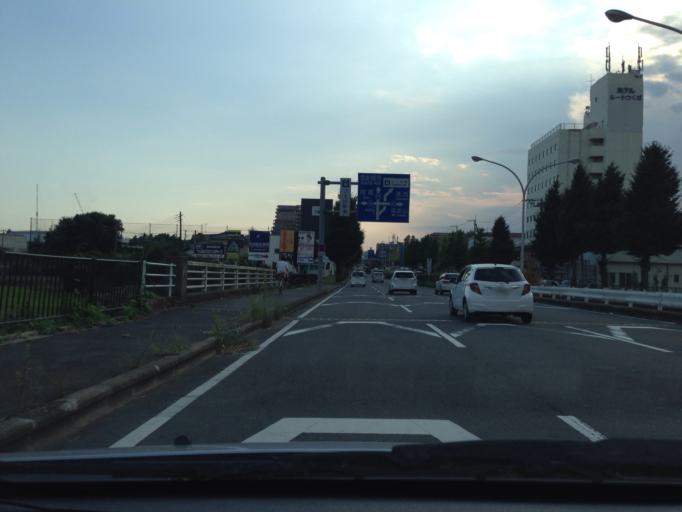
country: JP
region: Ibaraki
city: Naka
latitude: 36.0864
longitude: 140.1273
